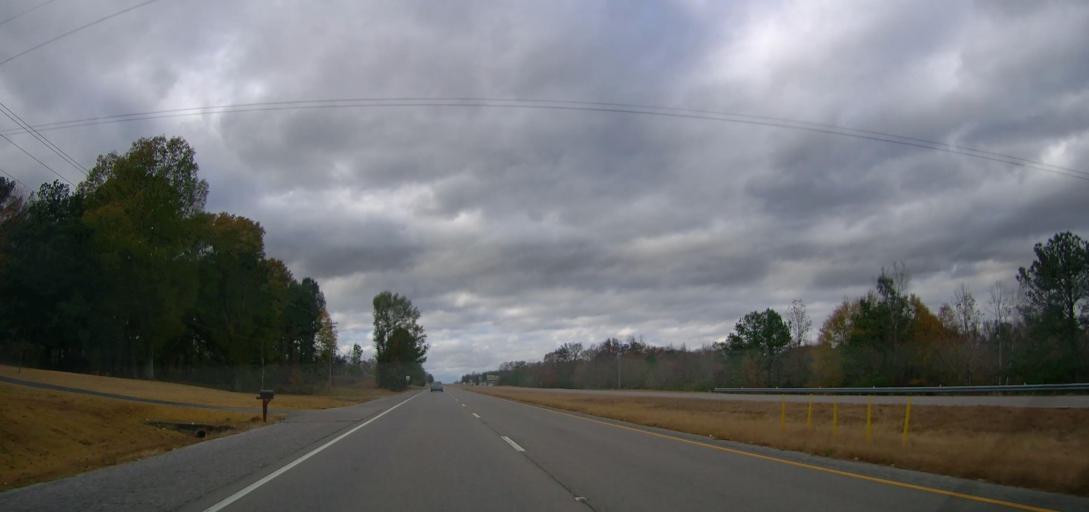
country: US
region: Alabama
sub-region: Lawrence County
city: Town Creek
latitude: 34.5845
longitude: -87.4169
